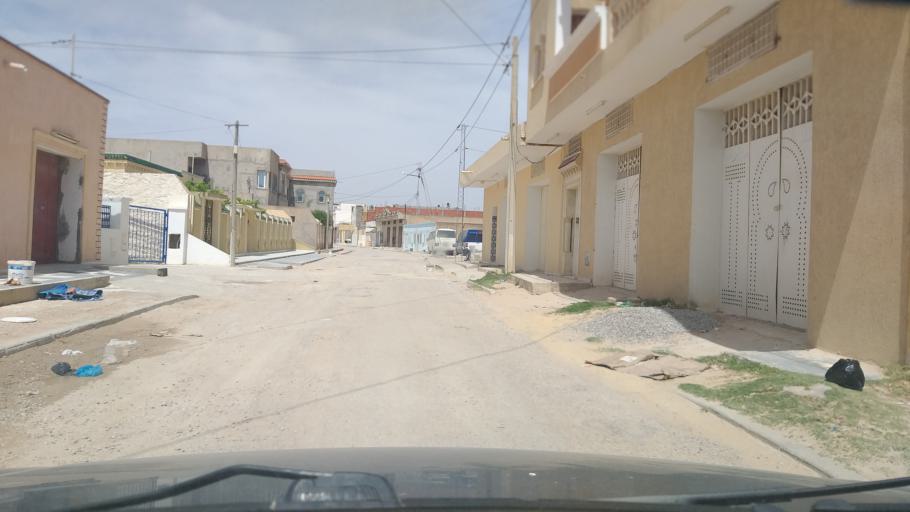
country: TN
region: Al Mahdiyah
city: El Jem
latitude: 35.2953
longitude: 10.6954
